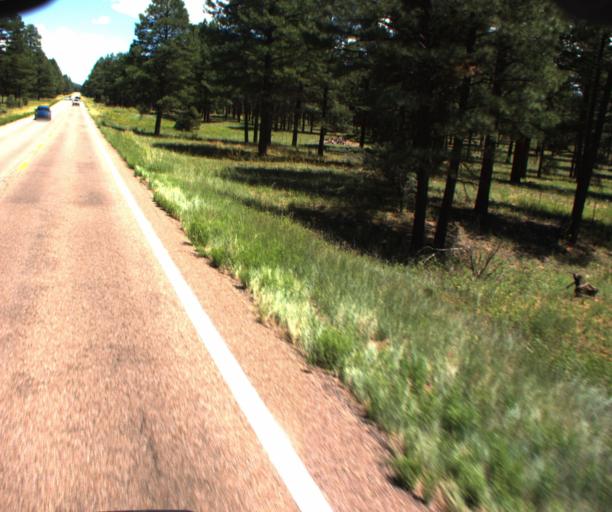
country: US
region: Arizona
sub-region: Navajo County
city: Lake of the Woods
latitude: 34.1207
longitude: -110.1270
